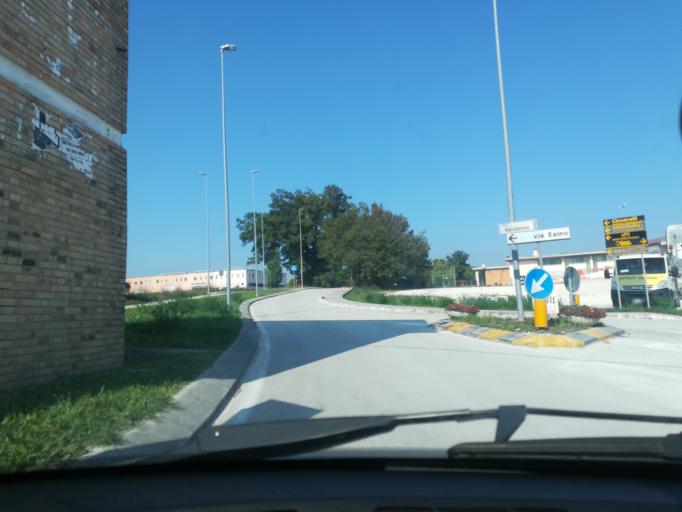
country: IT
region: The Marches
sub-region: Provincia di Macerata
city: Piediripa
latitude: 43.2710
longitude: 13.4701
